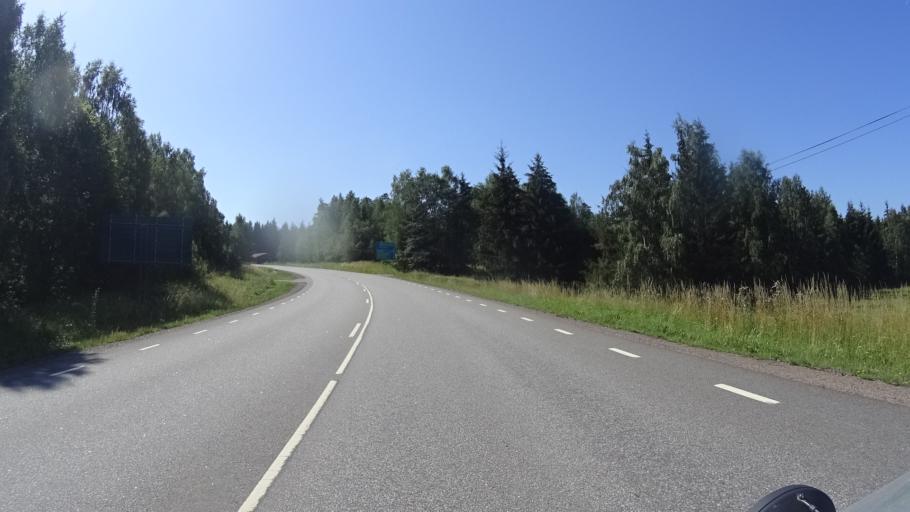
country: SE
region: OEstergoetland
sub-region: Vadstena Kommun
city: Herrestad
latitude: 58.3004
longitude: 14.9200
